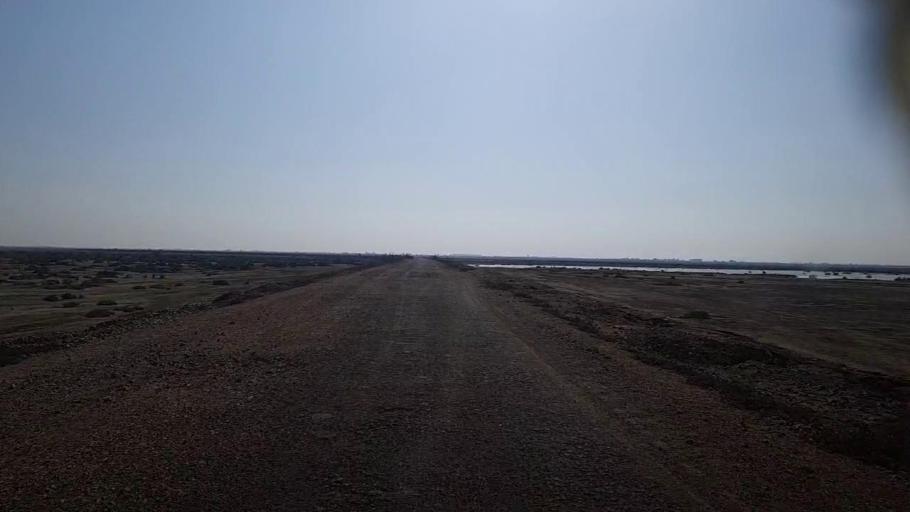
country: PK
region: Sindh
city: Mirpur Sakro
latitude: 24.5191
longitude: 67.4908
